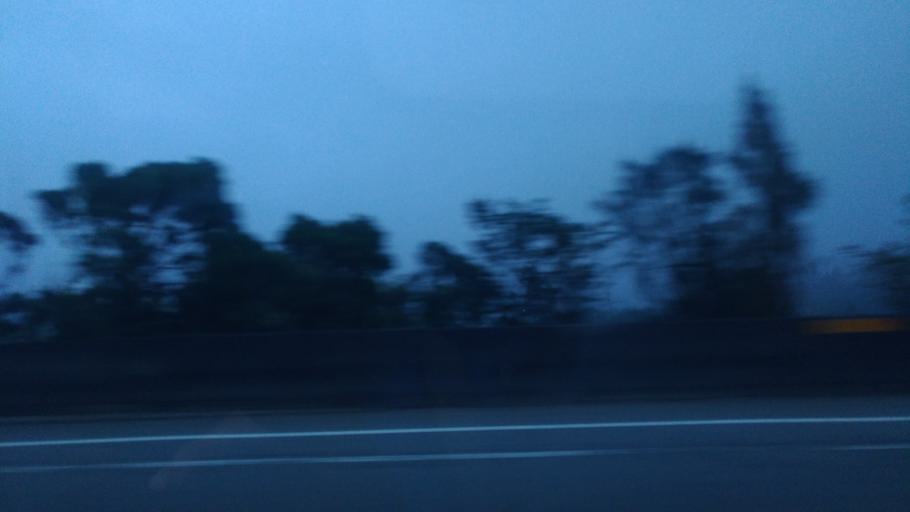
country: TW
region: Taiwan
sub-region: Miaoli
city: Miaoli
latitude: 24.5765
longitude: 120.7203
